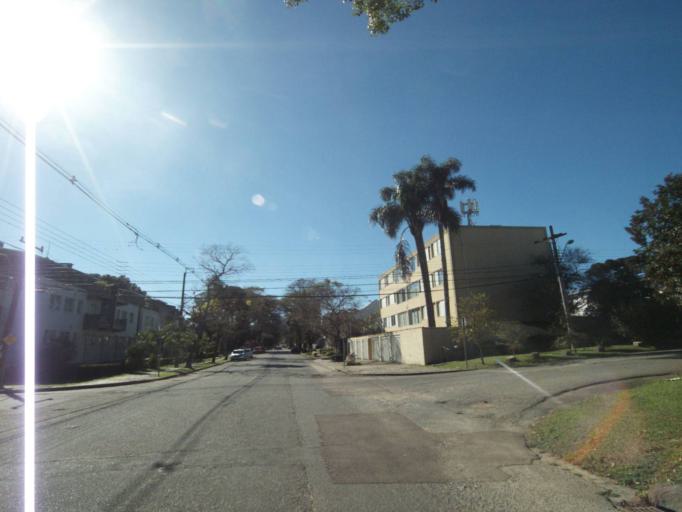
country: BR
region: Parana
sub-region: Curitiba
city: Curitiba
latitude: -25.4152
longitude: -49.2452
